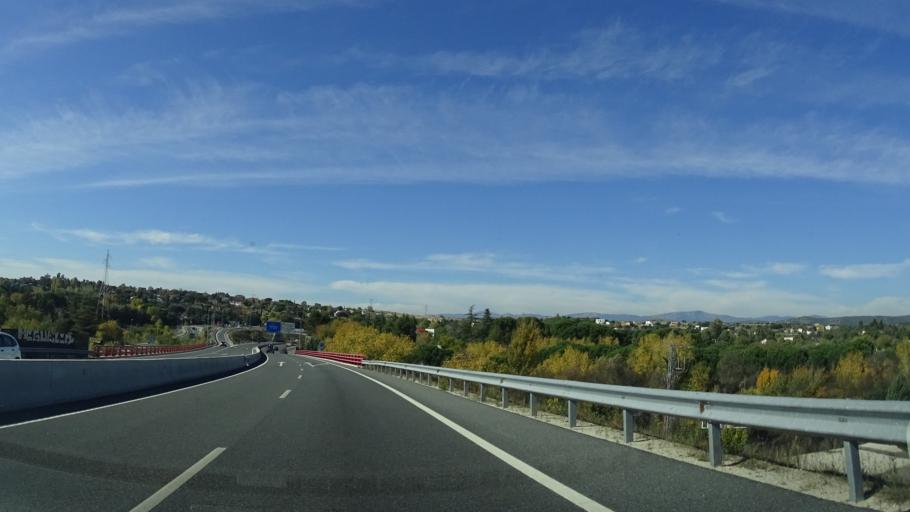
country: ES
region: Madrid
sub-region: Provincia de Madrid
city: Villanueva del Pardillo
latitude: 40.4850
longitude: -3.9357
